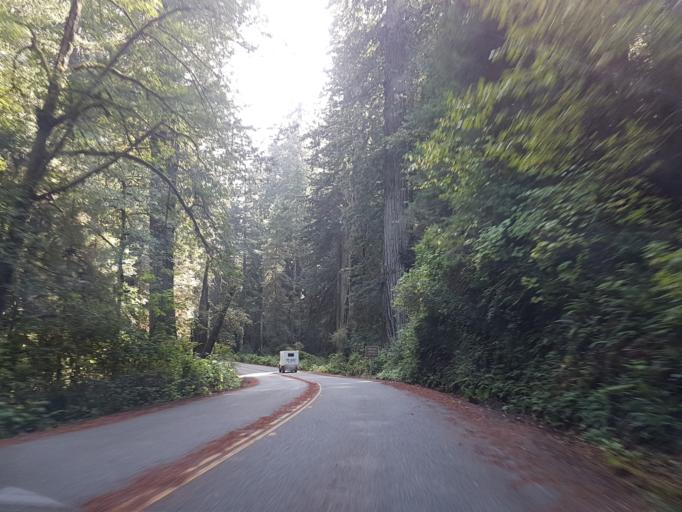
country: US
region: California
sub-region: Del Norte County
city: Bertsch-Oceanview
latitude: 41.4409
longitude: -124.0411
